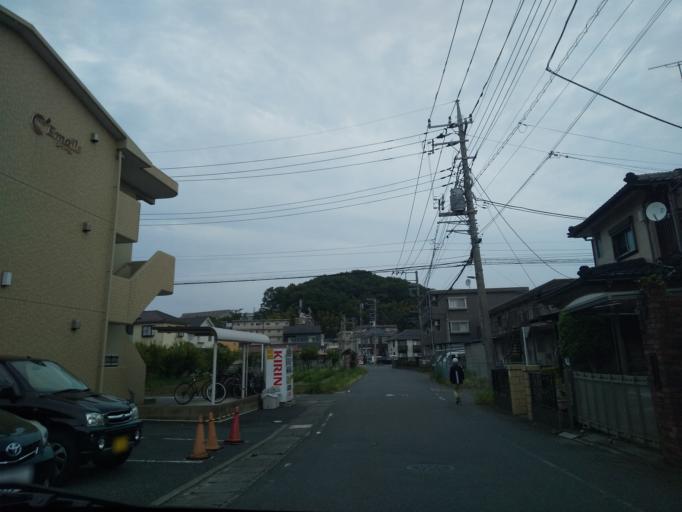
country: JP
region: Tokyo
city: Hachioji
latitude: 35.5987
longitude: 139.3589
